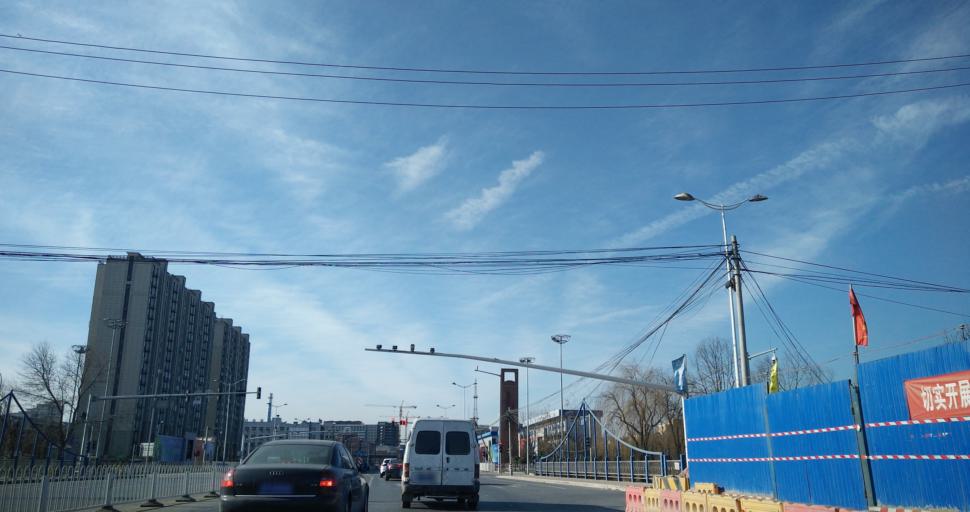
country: CN
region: Beijing
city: Xingfeng
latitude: 39.7416
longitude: 116.3446
